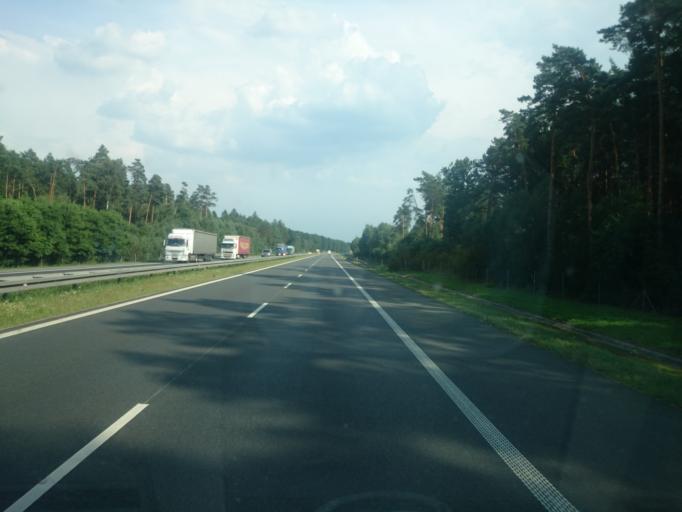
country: PL
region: Opole Voivodeship
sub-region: Powiat opolski
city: Proszkow
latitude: 50.5583
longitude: 17.8793
